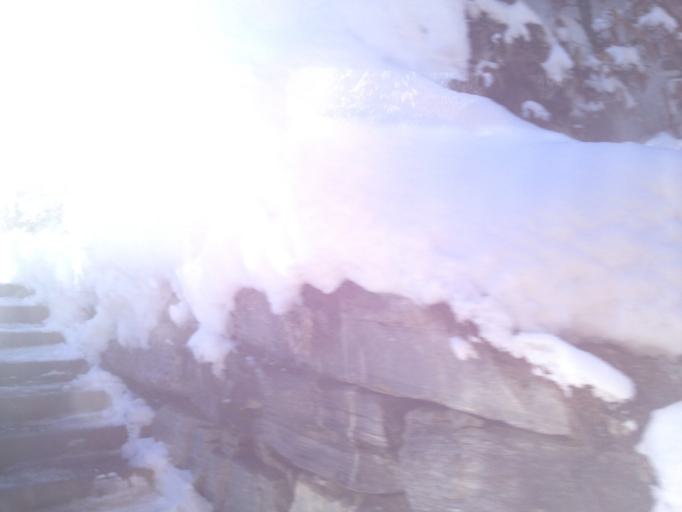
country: CH
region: Grisons
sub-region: Praettigau/Davos District
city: Klosters Serneus
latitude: 46.8625
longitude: 9.8918
